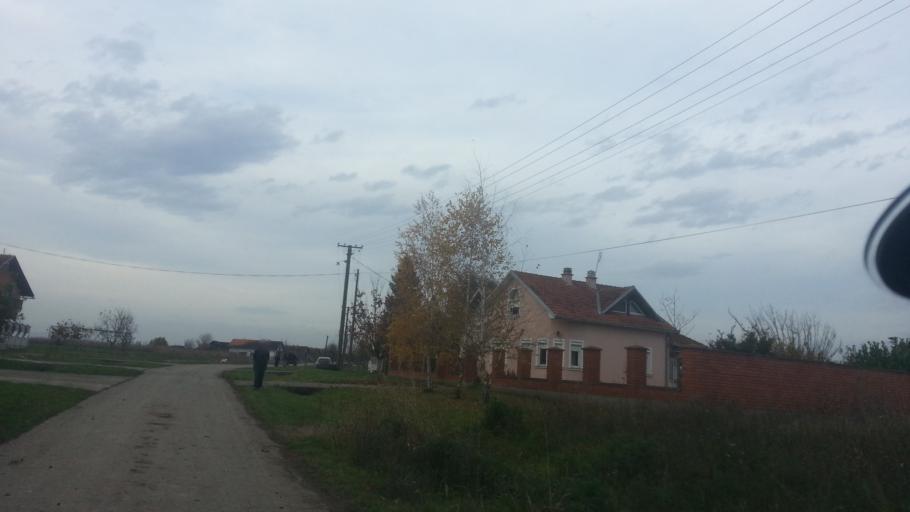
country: RS
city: Putinci
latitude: 44.9687
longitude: 19.9697
